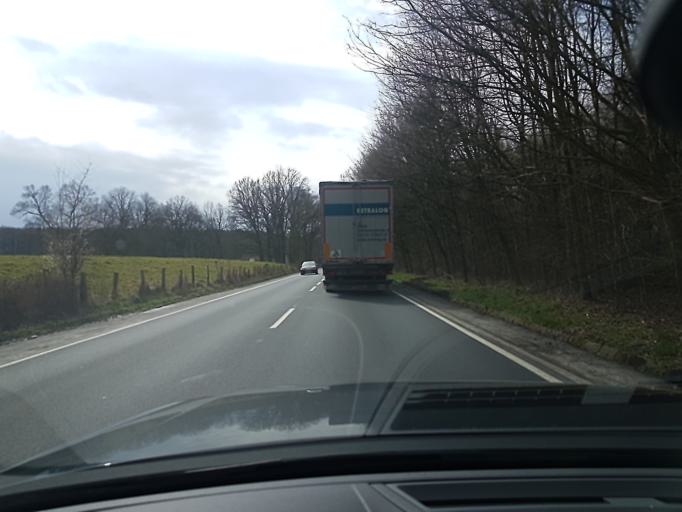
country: DE
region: North Rhine-Westphalia
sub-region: Regierungsbezirk Arnsberg
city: Frondenberg
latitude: 51.4658
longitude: 7.7072
